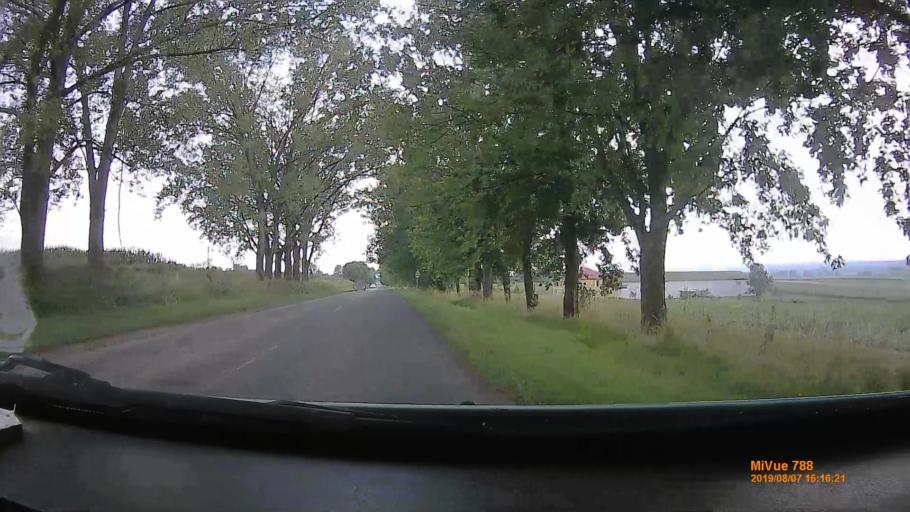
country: HU
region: Borsod-Abauj-Zemplen
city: Gonc
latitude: 48.4625
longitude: 21.2492
